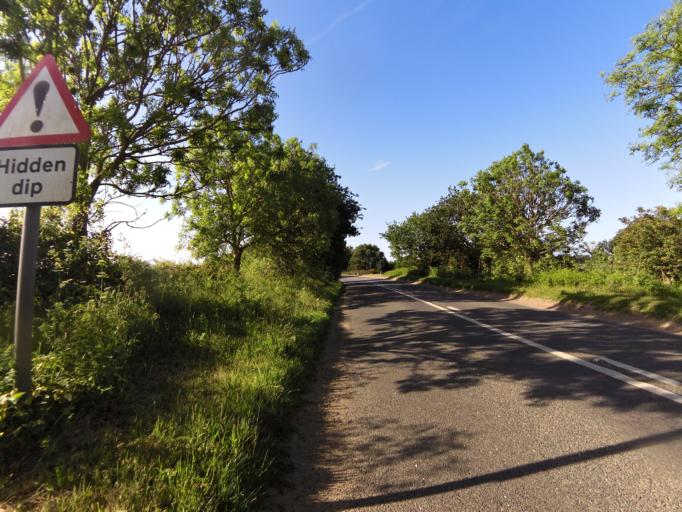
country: GB
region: England
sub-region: Suffolk
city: Woodbridge
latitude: 52.0772
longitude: 1.3636
